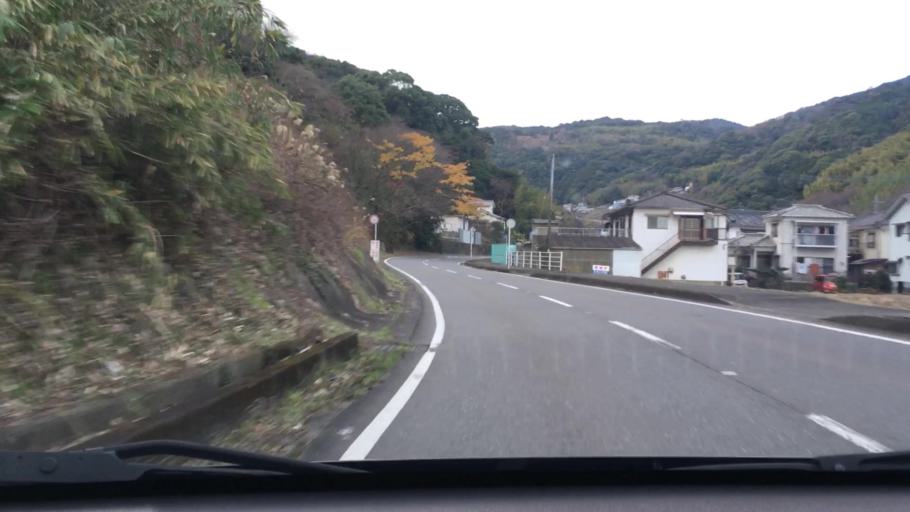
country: JP
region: Oita
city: Hiji
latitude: 33.3603
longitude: 131.4930
